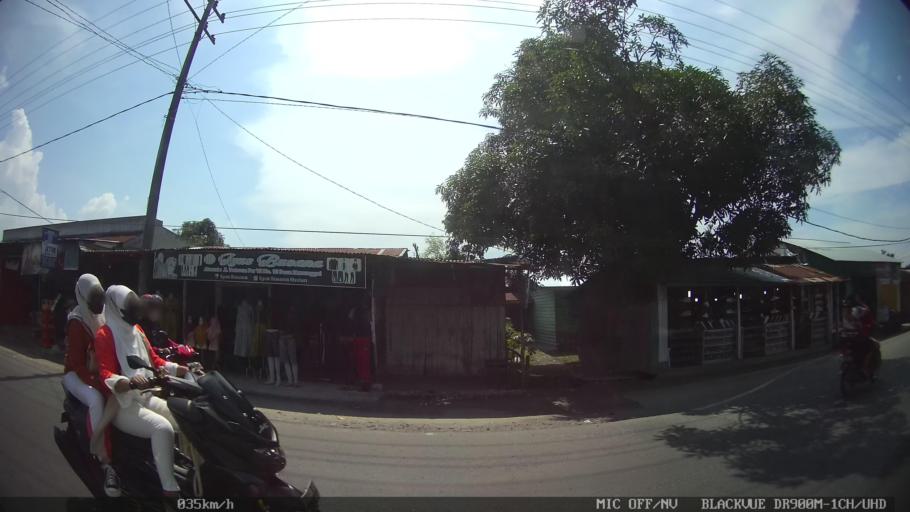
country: ID
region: North Sumatra
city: Medan
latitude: 3.6482
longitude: 98.6573
